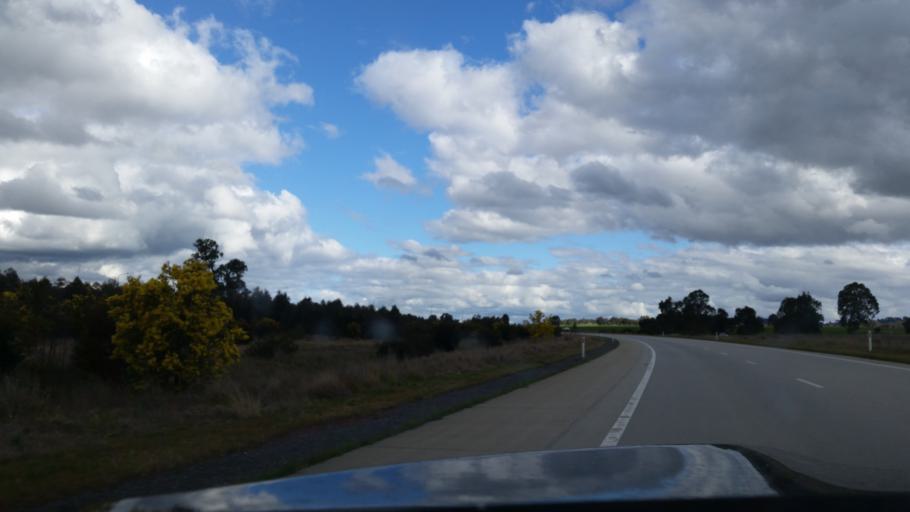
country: AU
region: New South Wales
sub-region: Greater Hume Shire
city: Jindera
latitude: -35.9316
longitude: 147.0034
